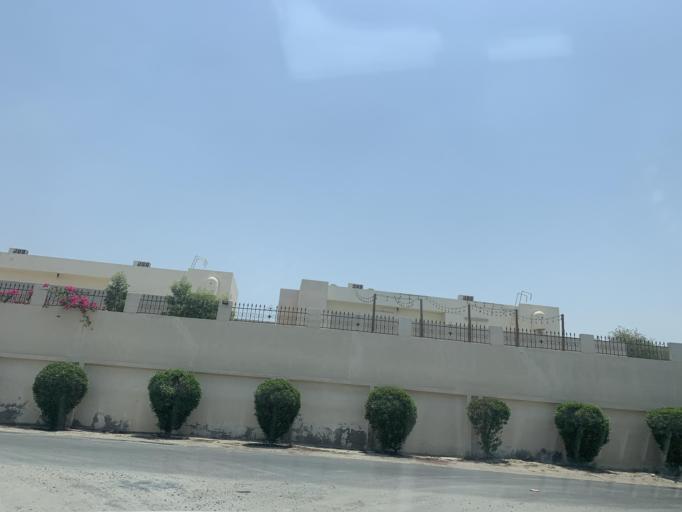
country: BH
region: Manama
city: Jidd Hafs
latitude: 26.2076
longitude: 50.4724
